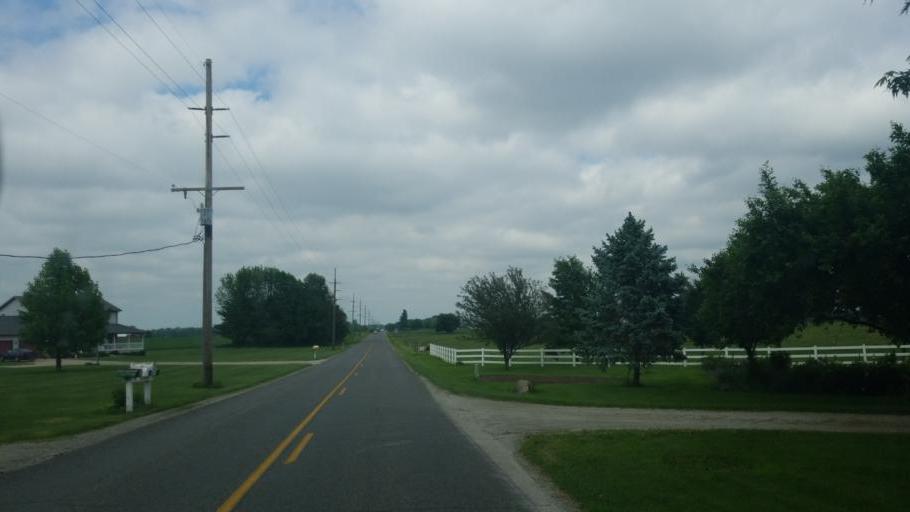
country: US
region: Indiana
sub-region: Elkhart County
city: Nappanee
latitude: 41.4798
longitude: -86.0482
